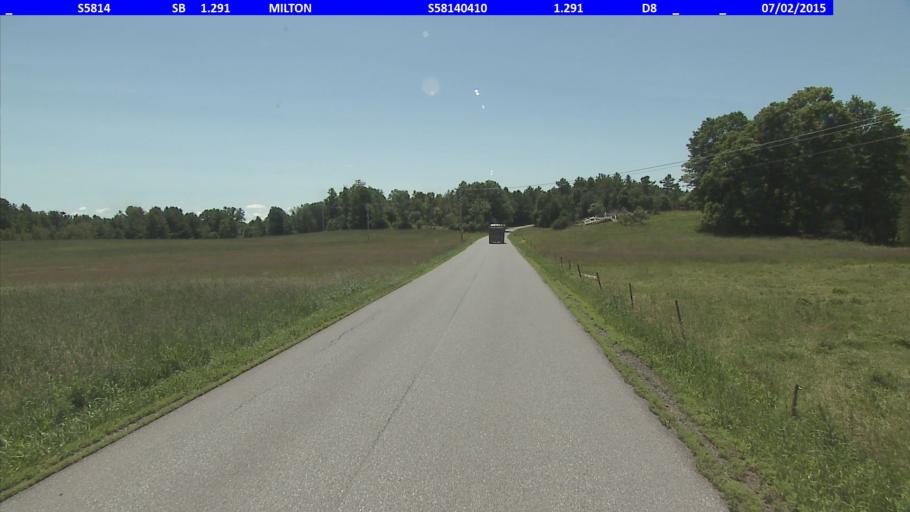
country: US
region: Vermont
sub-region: Chittenden County
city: Milton
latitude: 44.6465
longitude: -73.1668
